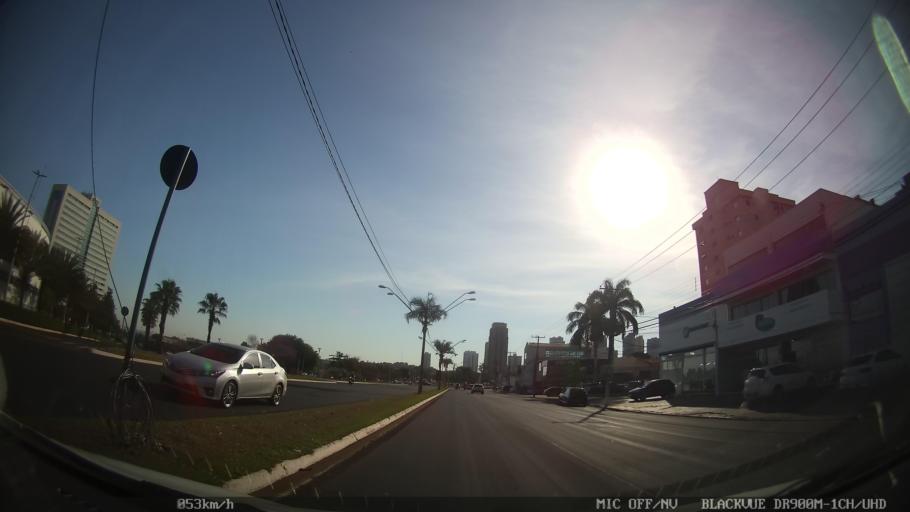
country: BR
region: Sao Paulo
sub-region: Ribeirao Preto
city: Ribeirao Preto
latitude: -21.2113
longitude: -47.8135
